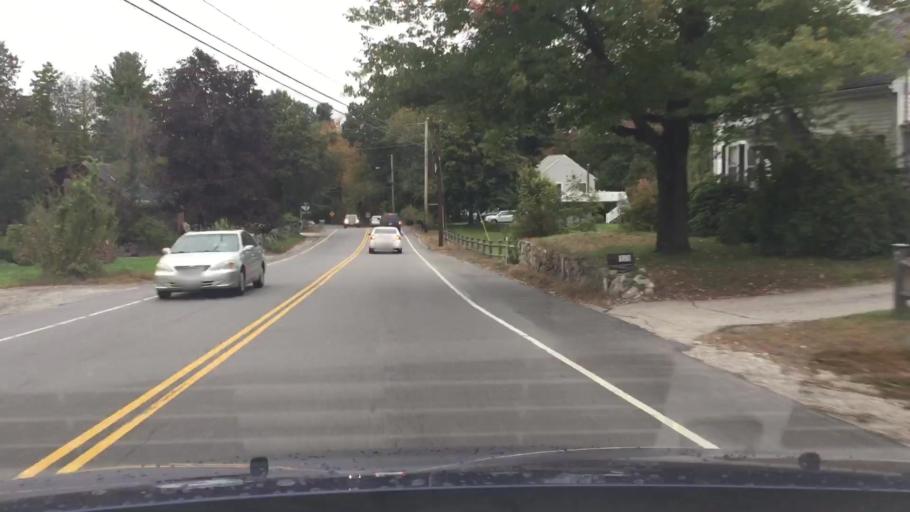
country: US
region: Massachusetts
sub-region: Middlesex County
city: Tyngsboro
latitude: 42.7014
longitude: -71.3895
